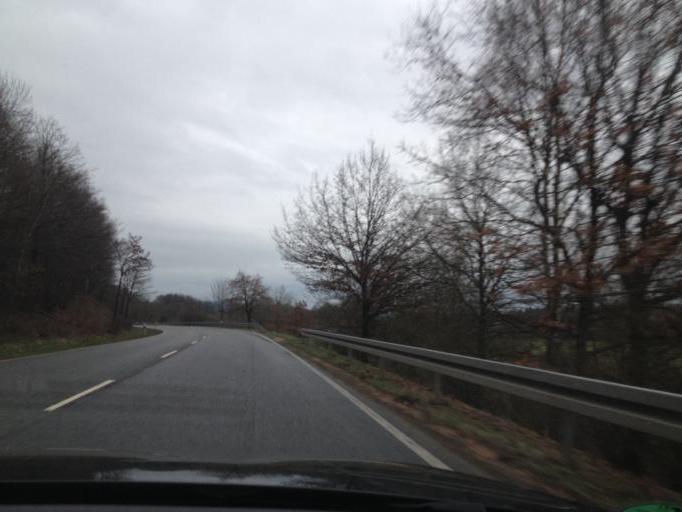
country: DE
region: Saarland
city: Nohfelden
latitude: 49.5773
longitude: 7.1616
